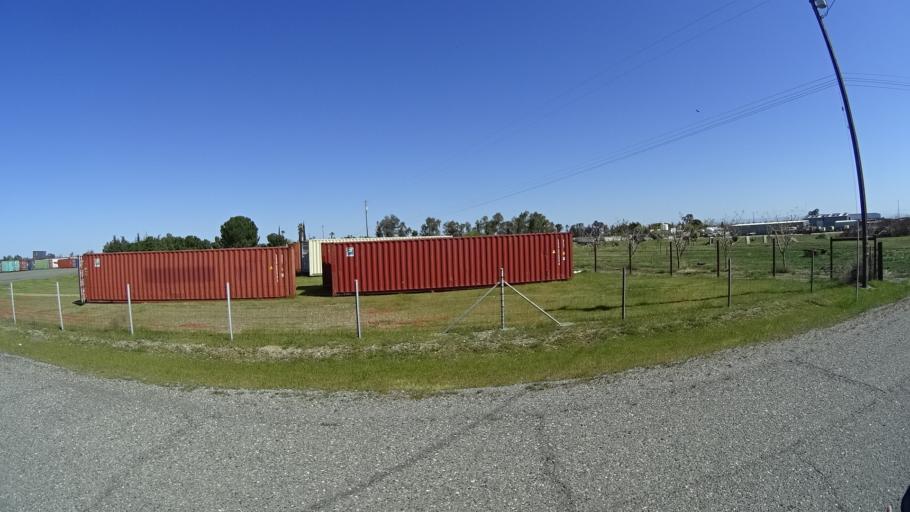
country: US
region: California
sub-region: Glenn County
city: Orland
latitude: 39.6975
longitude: -122.2039
